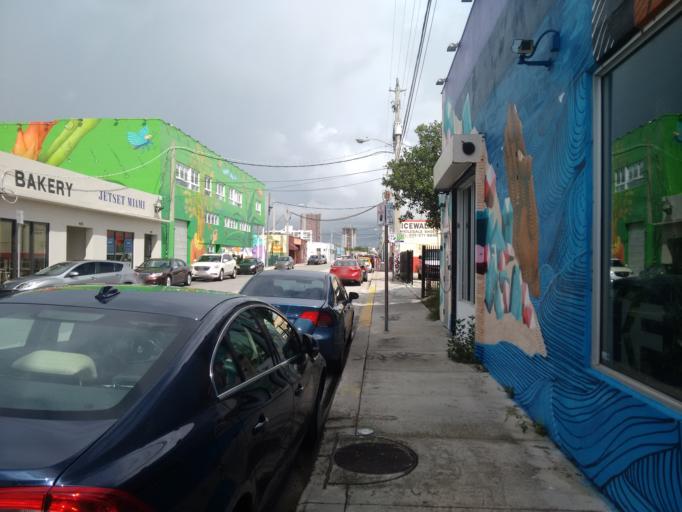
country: US
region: Florida
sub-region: Miami-Dade County
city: Allapattah
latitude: 25.8013
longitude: -80.2023
